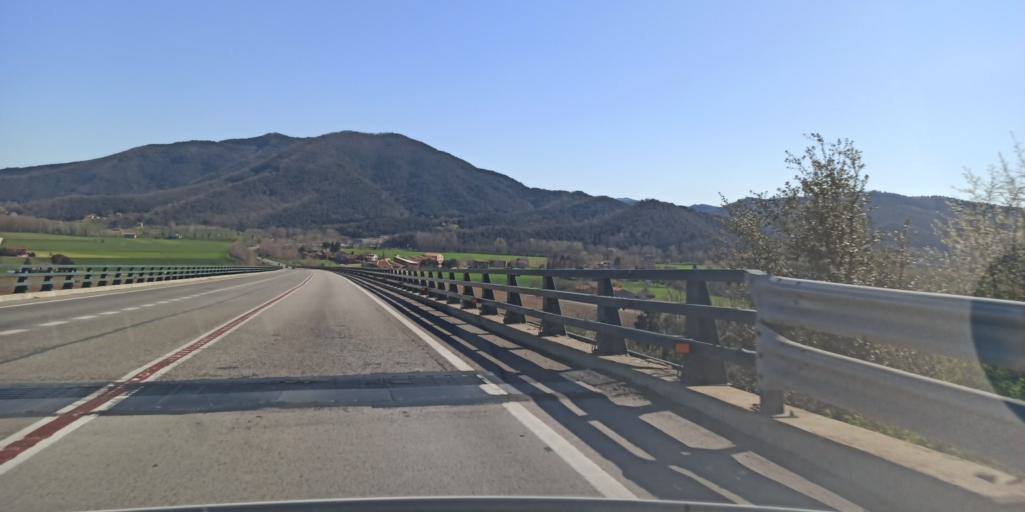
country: ES
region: Catalonia
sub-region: Provincia de Girona
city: Bas
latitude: 42.1253
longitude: 2.4325
